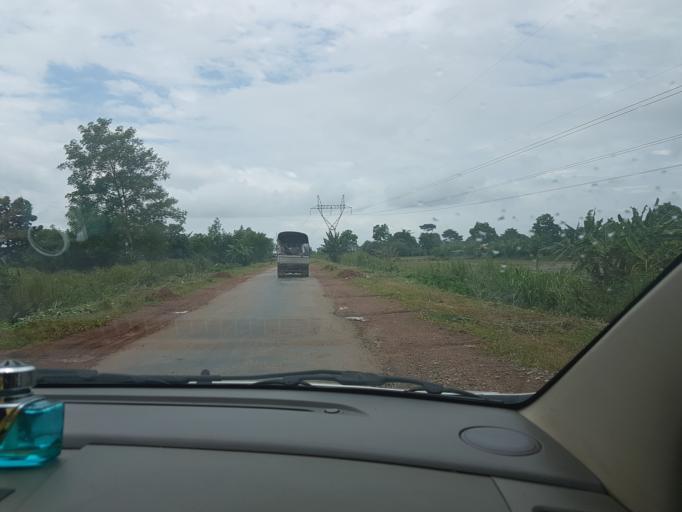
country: MM
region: Bago
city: Nyaunglebin
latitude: 17.9284
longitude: 96.8177
